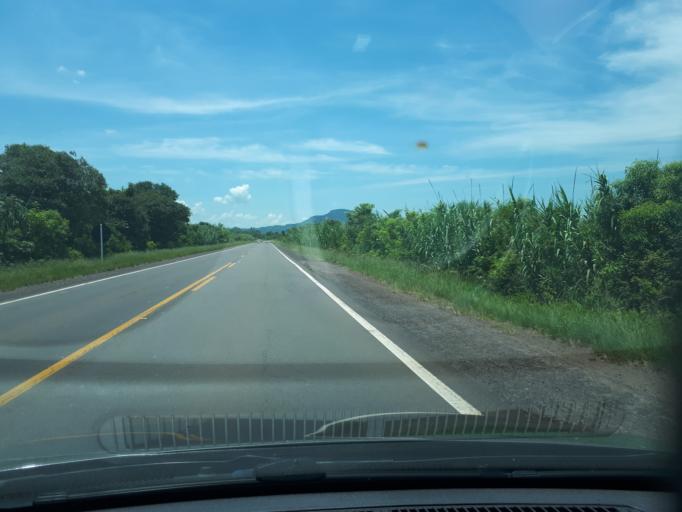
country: BR
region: Rio Grande do Sul
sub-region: Candelaria
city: Candelaria
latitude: -29.7266
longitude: -52.9329
